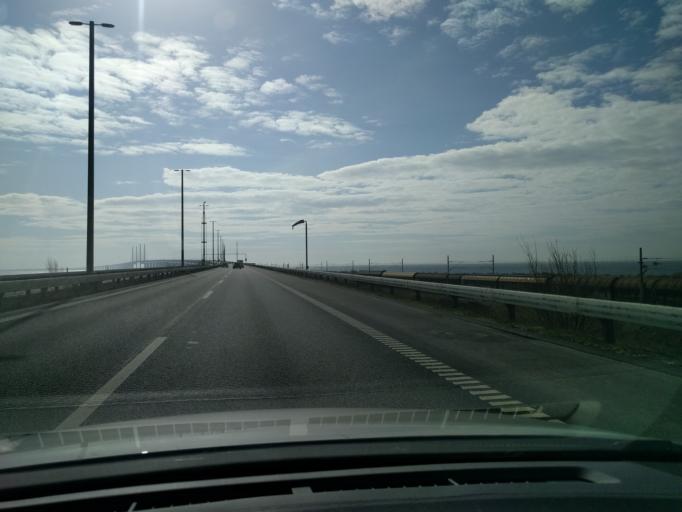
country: DK
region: Capital Region
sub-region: Dragor Kommune
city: Dragor
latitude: 55.5948
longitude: 12.7622
